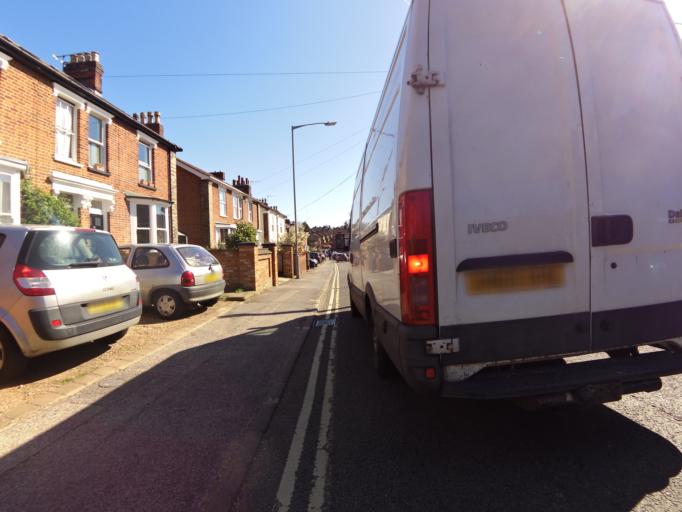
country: GB
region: England
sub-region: Suffolk
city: Ipswich
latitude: 52.0579
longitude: 1.1685
